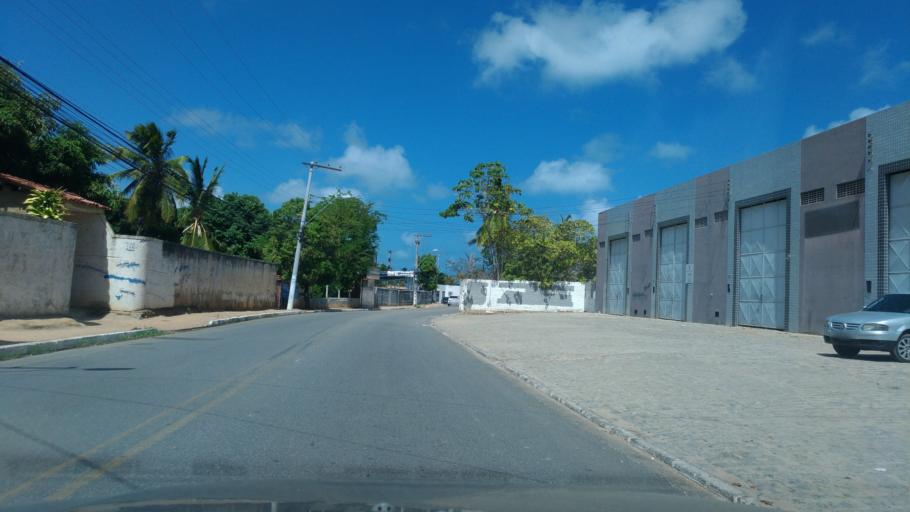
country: BR
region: Alagoas
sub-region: Maceio
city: Maceio
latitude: -9.6198
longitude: -35.7084
